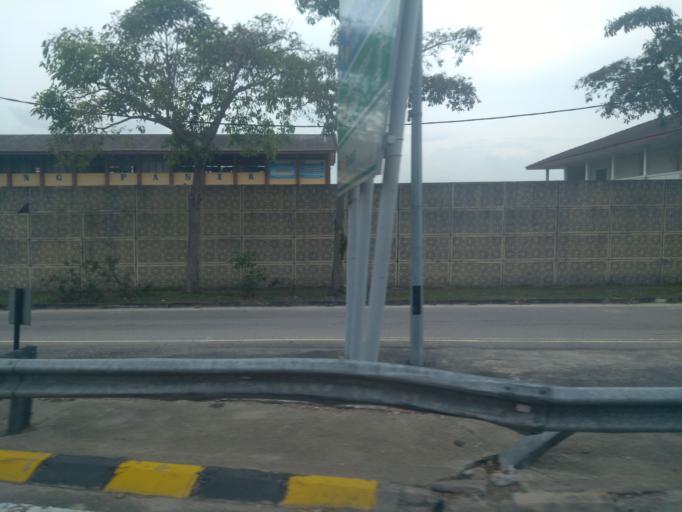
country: MY
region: Johor
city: Skudai
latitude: 1.4991
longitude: 103.6979
